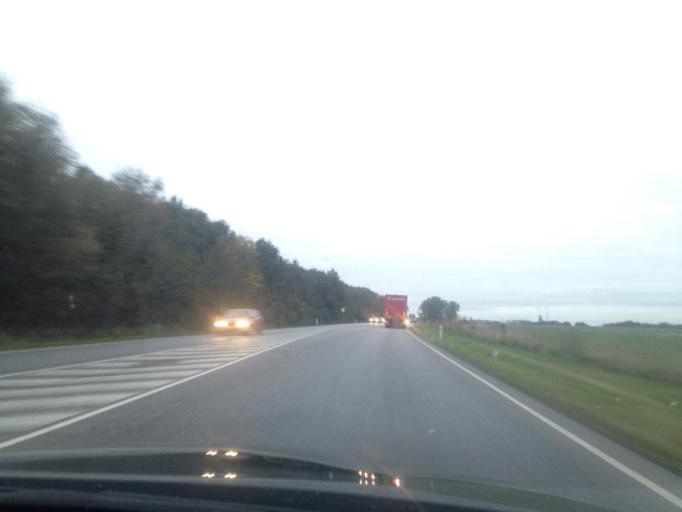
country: DK
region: Zealand
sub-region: Roskilde Kommune
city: Vindinge
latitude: 55.6028
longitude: 12.1005
